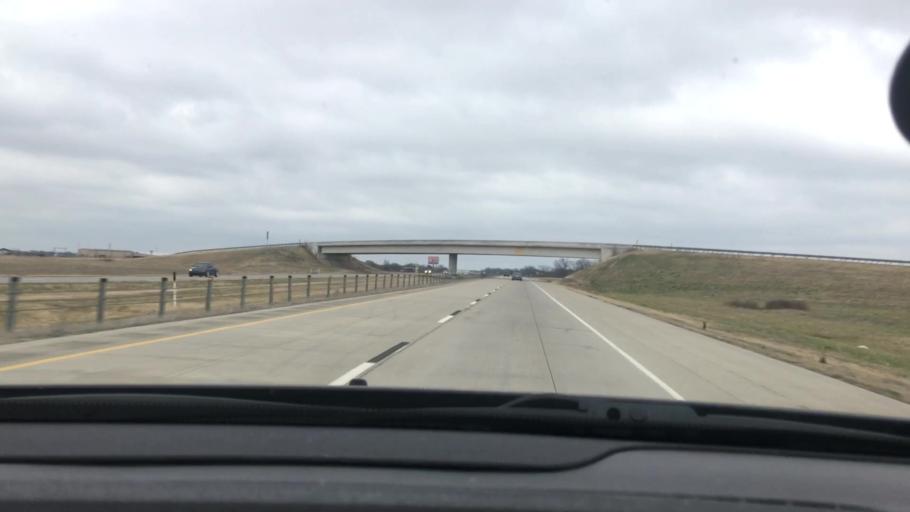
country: US
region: Oklahoma
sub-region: Bryan County
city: Durant
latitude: 34.0927
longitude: -96.3222
